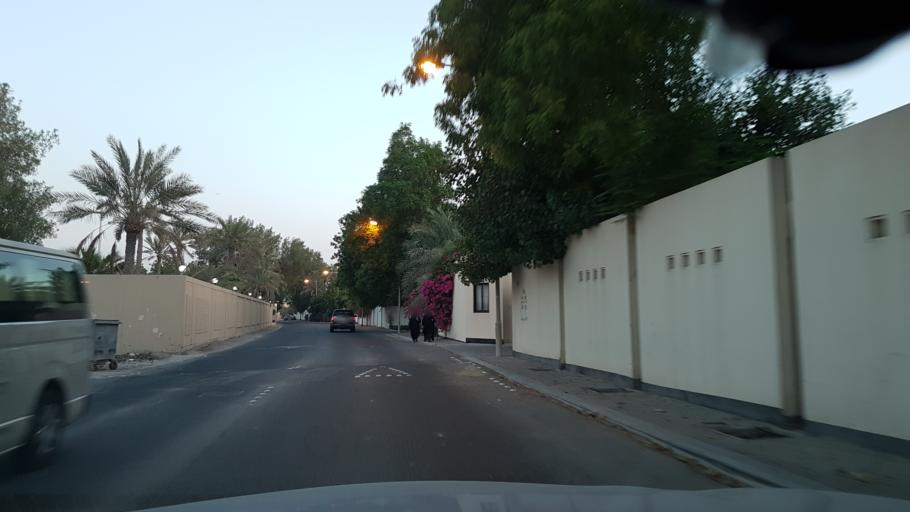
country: BH
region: Manama
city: Jidd Hafs
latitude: 26.2268
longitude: 50.4889
